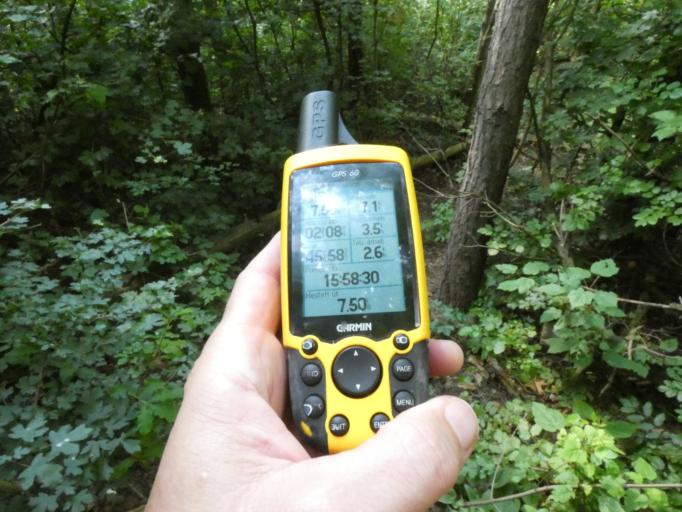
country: HU
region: Nograd
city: Szurdokpuspoki
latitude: 47.8525
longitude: 19.7108
